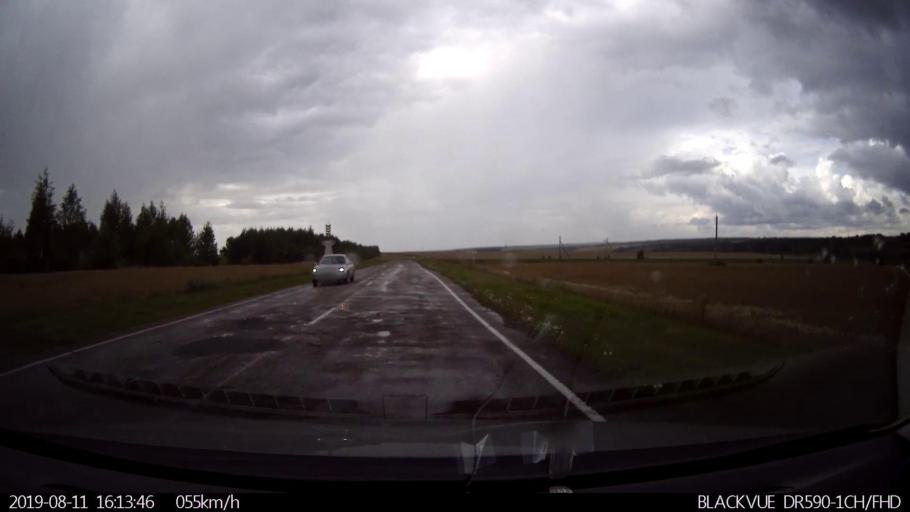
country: RU
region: Ulyanovsk
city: Ignatovka
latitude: 54.0227
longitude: 47.6359
